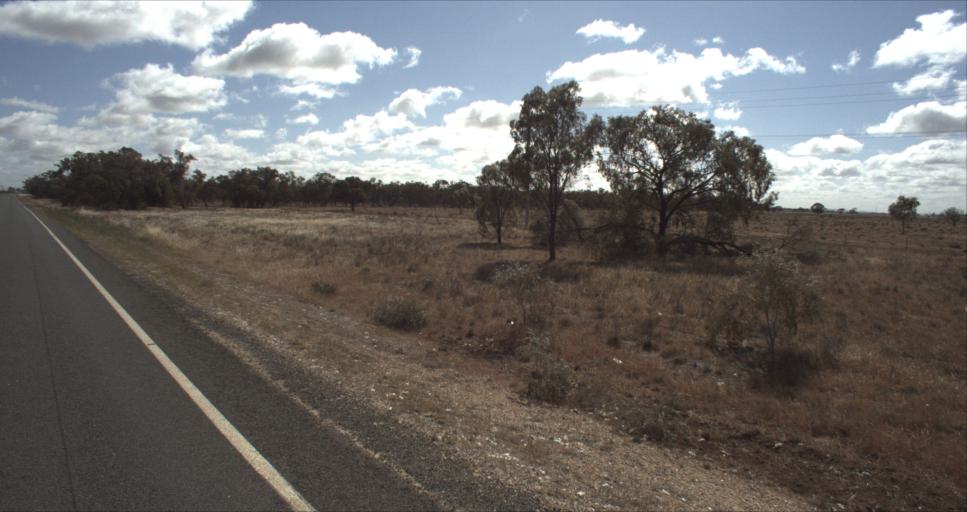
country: AU
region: New South Wales
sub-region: Murrumbidgee Shire
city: Darlington Point
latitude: -34.5267
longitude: 146.1747
